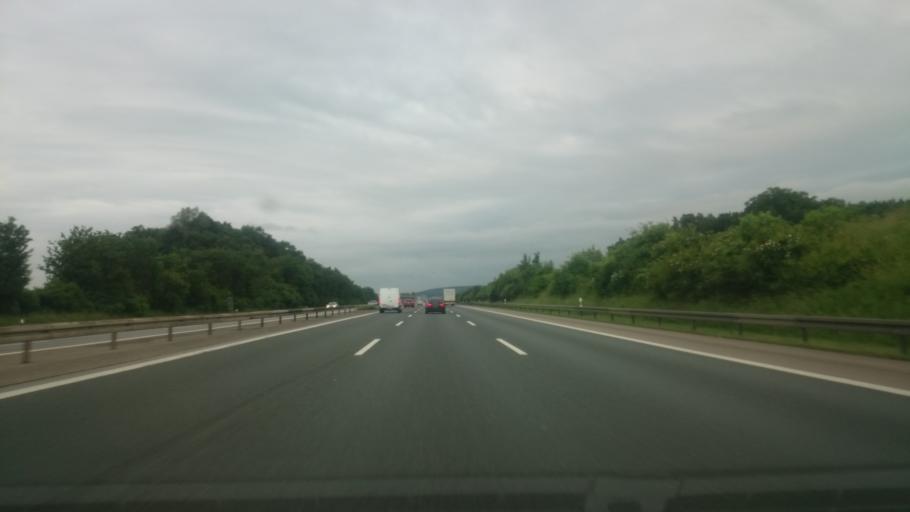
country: DE
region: Bavaria
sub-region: Upper Palatinate
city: Freystadt
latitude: 49.1588
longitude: 11.2644
